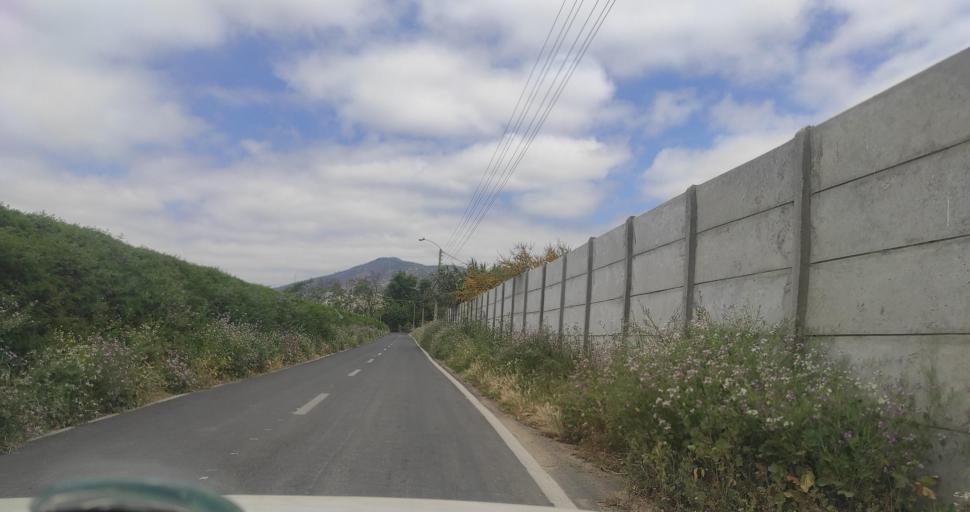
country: CL
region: Valparaiso
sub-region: Provincia de Marga Marga
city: Limache
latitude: -33.0360
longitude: -71.2315
